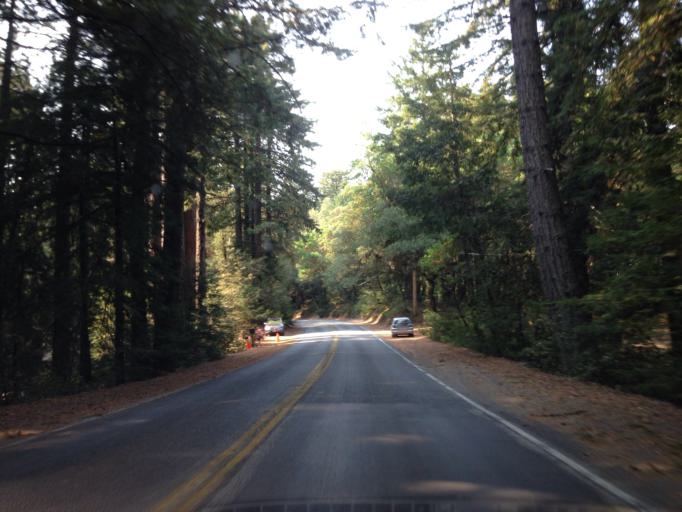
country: US
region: California
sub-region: San Mateo County
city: Emerald Lake Hills
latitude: 37.4335
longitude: -122.3163
